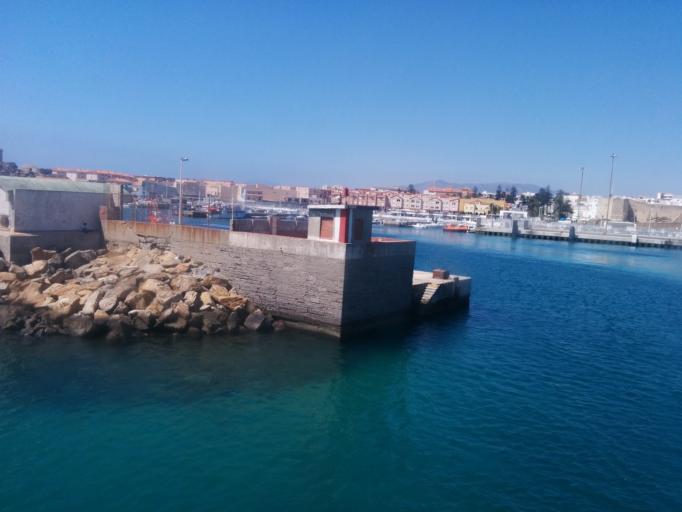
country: ES
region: Andalusia
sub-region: Provincia de Cadiz
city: Tarifa
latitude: 36.0083
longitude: -5.6023
